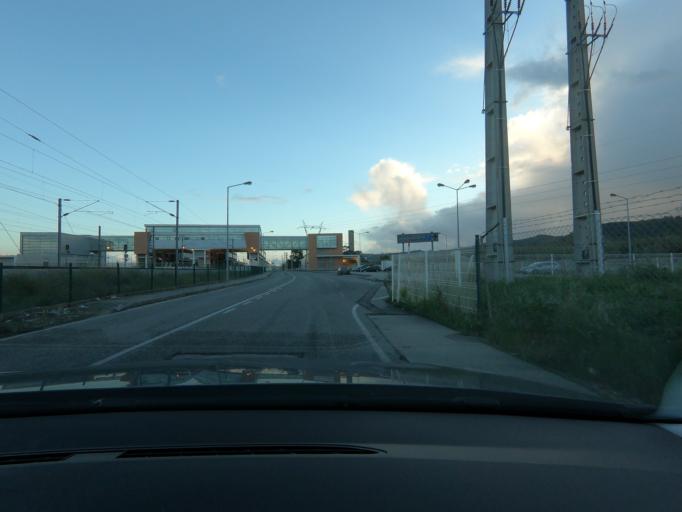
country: PT
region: Lisbon
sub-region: Vila Franca de Xira
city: Castanheira do Ribatejo
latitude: 38.9902
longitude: -8.9649
